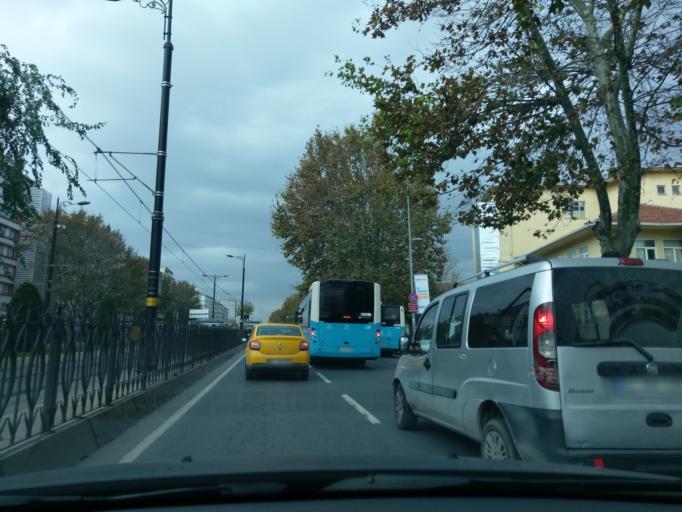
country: TR
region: Istanbul
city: Istanbul
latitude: 41.0148
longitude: 28.9344
